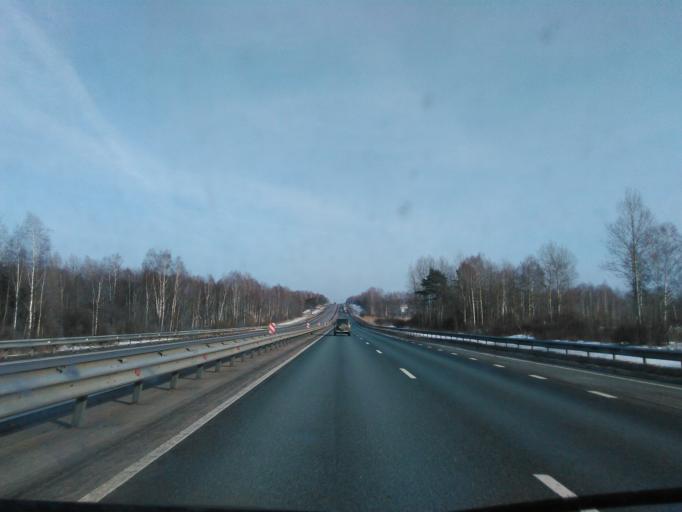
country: RU
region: Smolensk
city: Verkhnedneprovskiy
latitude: 55.1824
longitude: 33.5330
